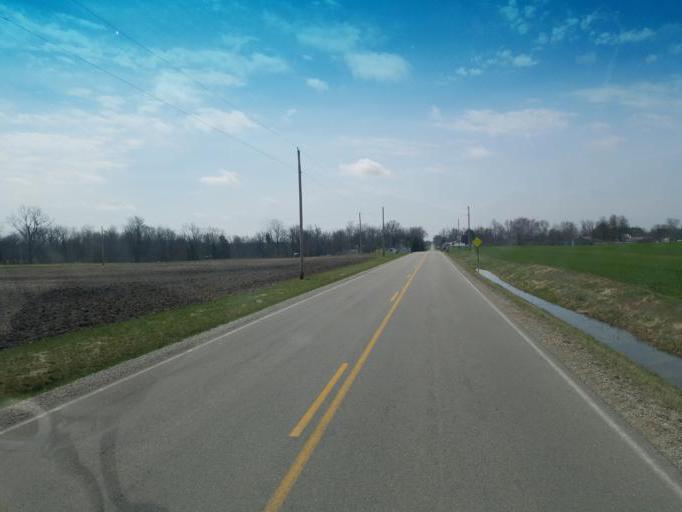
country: US
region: Ohio
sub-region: Crawford County
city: Bucyrus
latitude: 40.9316
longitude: -83.0933
